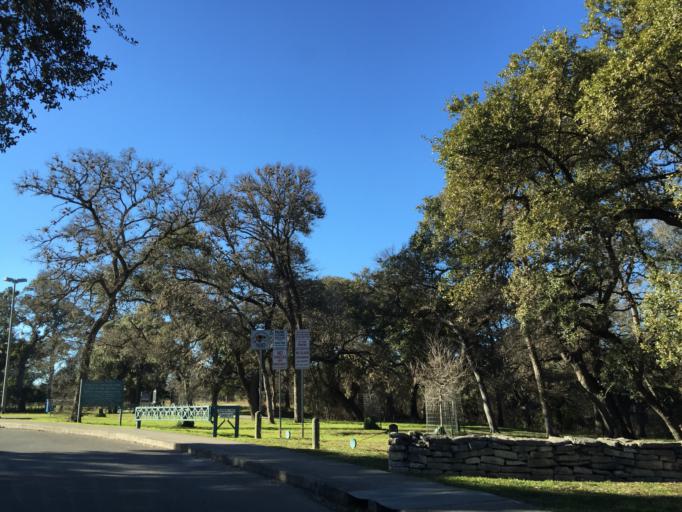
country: US
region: Texas
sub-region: Bexar County
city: Castle Hills
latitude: 29.5563
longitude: -98.4990
